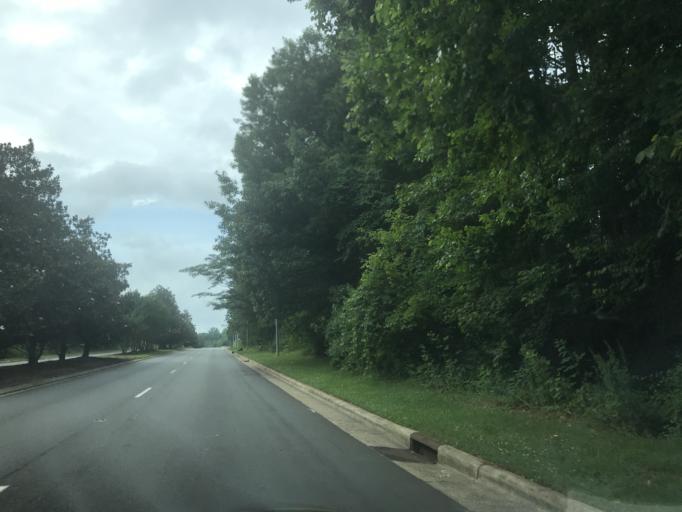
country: US
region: North Carolina
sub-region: Wake County
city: Cary
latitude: 35.7966
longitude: -78.7642
